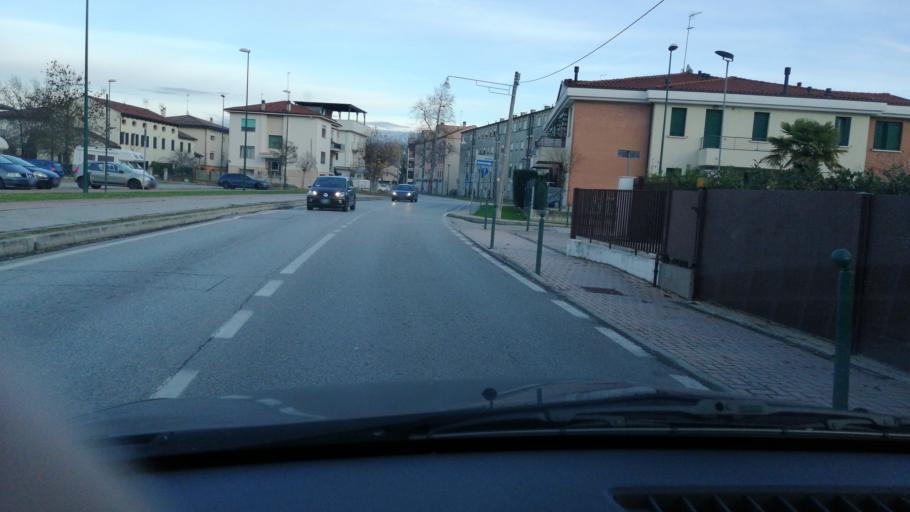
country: IT
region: Veneto
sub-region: Provincia di Venezia
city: Zelarino
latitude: 45.4929
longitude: 12.2112
